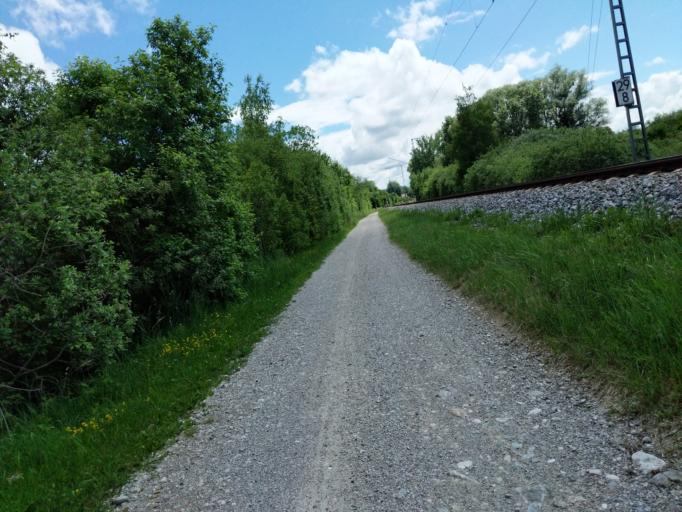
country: DE
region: Bavaria
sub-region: Upper Bavaria
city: Herrsching am Ammersee
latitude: 48.0081
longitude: 11.1726
